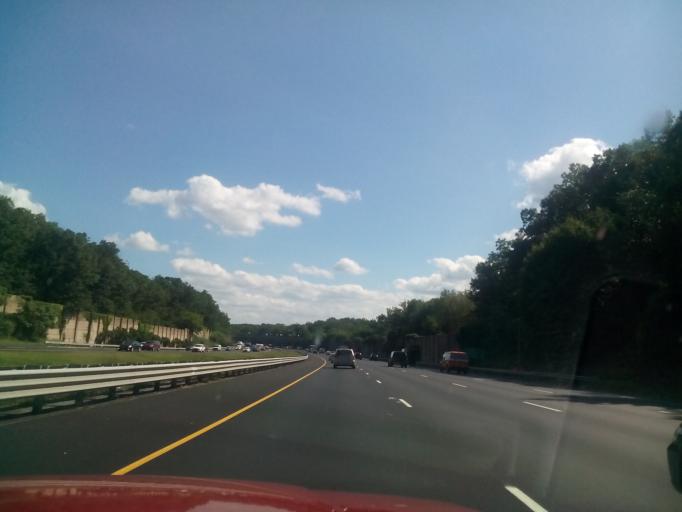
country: US
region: New Jersey
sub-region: Morris County
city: Mountain Lakes
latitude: 40.8818
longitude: -74.4696
